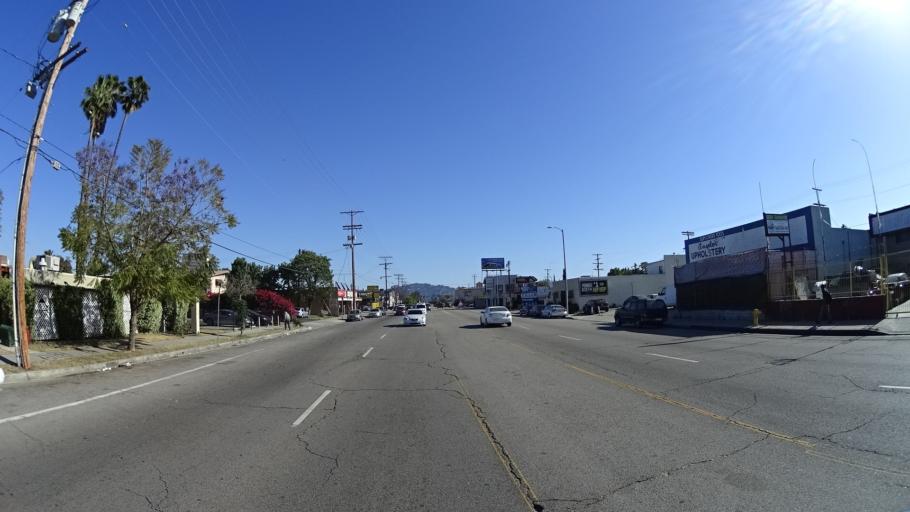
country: US
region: California
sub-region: Los Angeles County
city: North Hollywood
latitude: 34.1821
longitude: -118.3702
